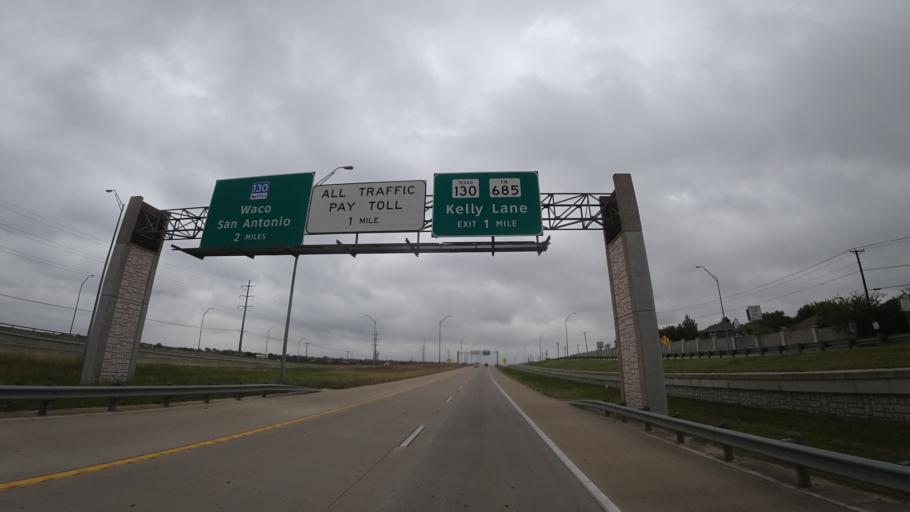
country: US
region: Texas
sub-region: Travis County
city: Windemere
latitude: 30.4886
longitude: -97.6339
